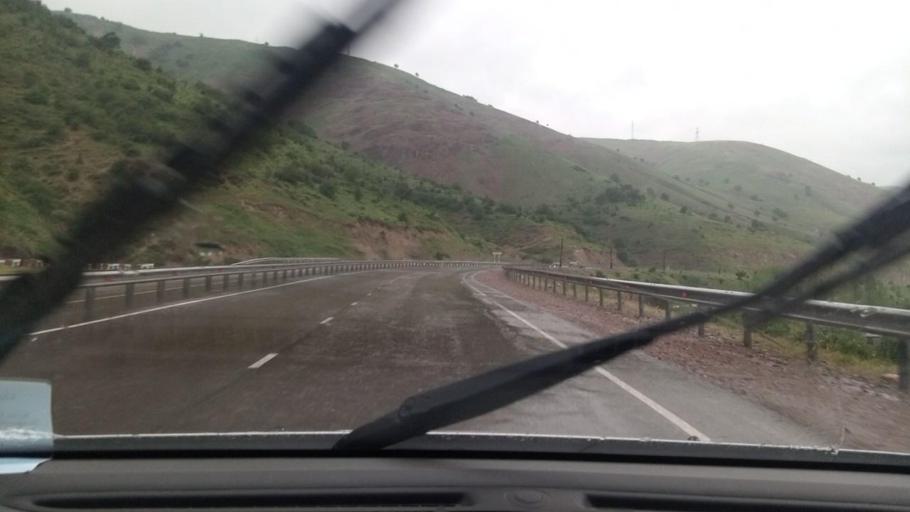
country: UZ
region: Toshkent
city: Angren
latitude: 41.0901
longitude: 70.3204
